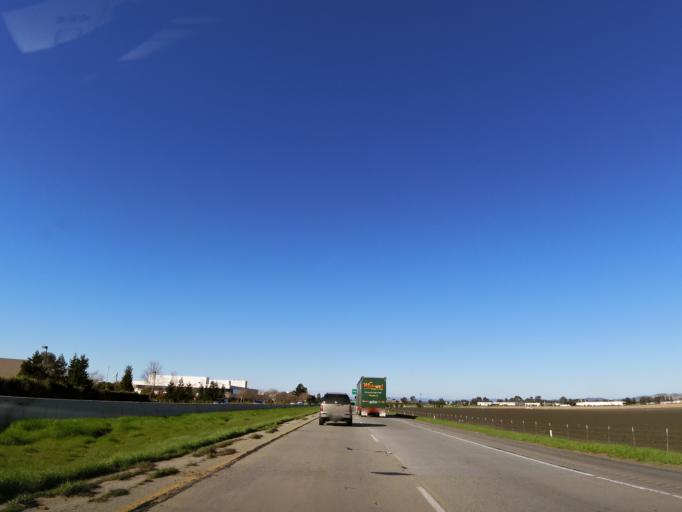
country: US
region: California
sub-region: Monterey County
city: Salinas
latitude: 36.6507
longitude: -121.6170
